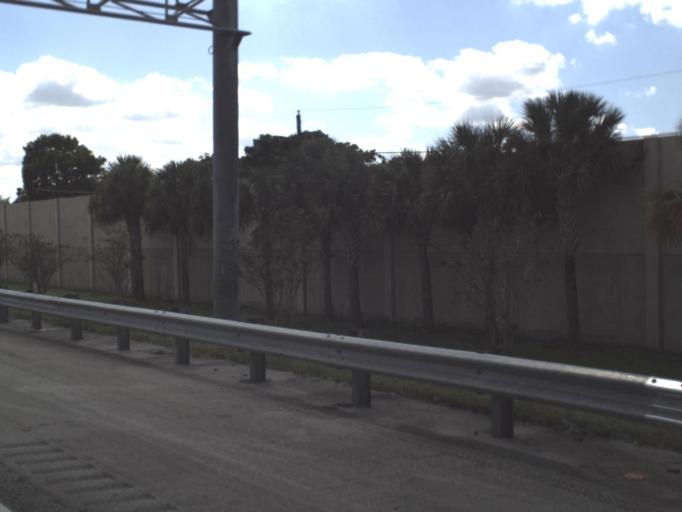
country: US
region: Florida
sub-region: Broward County
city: Lauderhill
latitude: 26.1495
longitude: -80.2196
